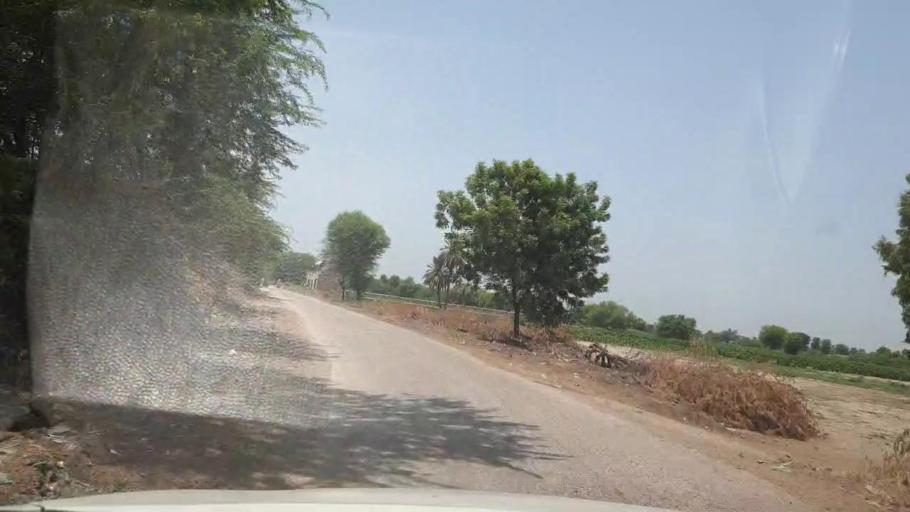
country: PK
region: Sindh
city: Bozdar
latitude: 27.1874
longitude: 68.6182
